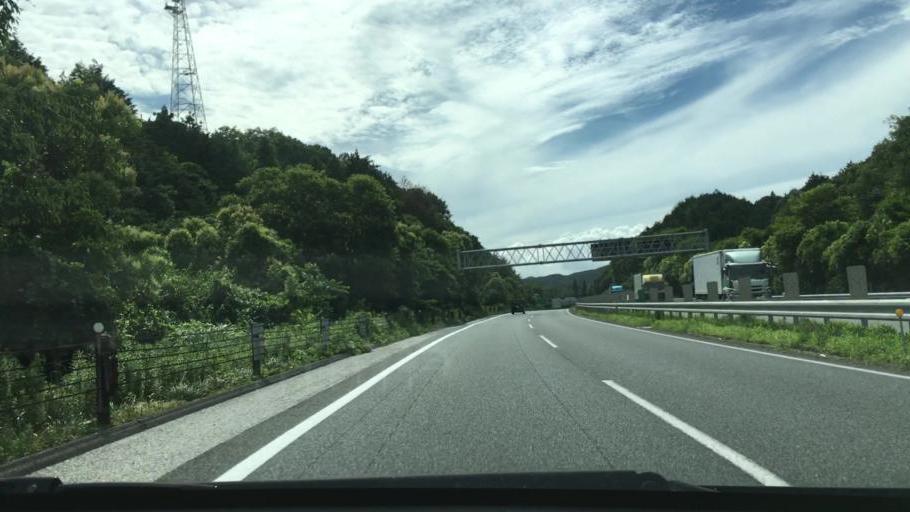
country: JP
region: Yamaguchi
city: Ogori-shimogo
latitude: 34.1258
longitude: 131.3923
